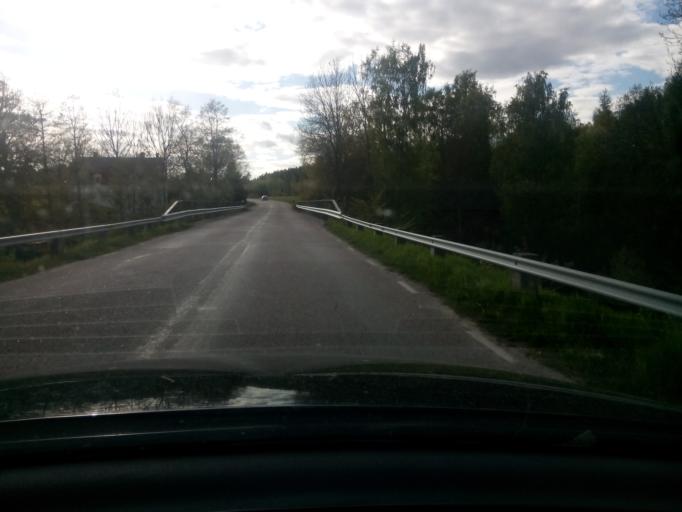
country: SE
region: Soedermanland
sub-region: Nykopings Kommun
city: Stigtomta
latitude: 58.9508
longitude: 16.8831
